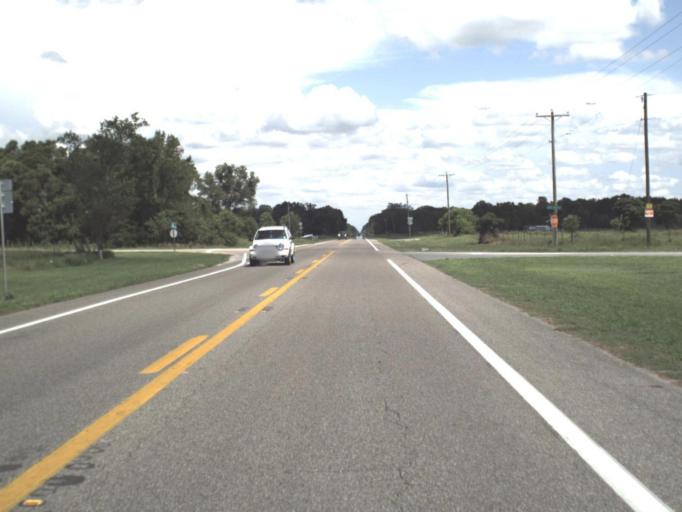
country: US
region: Florida
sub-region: Lafayette County
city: Mayo
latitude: 30.0393
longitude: -83.0712
